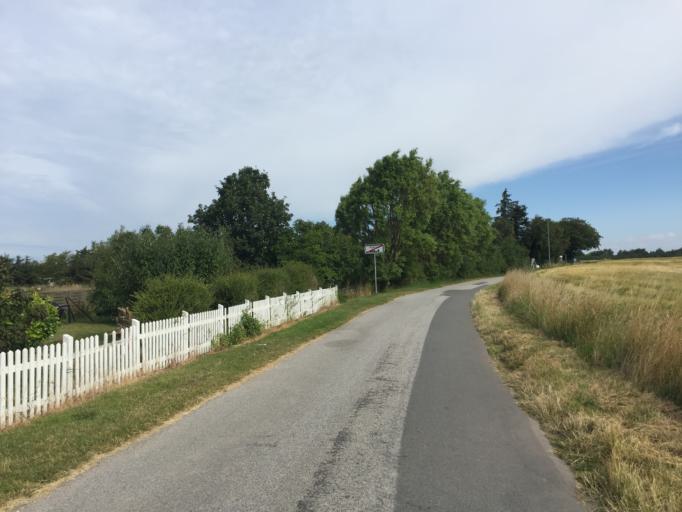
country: DK
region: Zealand
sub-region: Slagelse Kommune
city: Skaelskor
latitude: 55.2165
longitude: 11.1862
